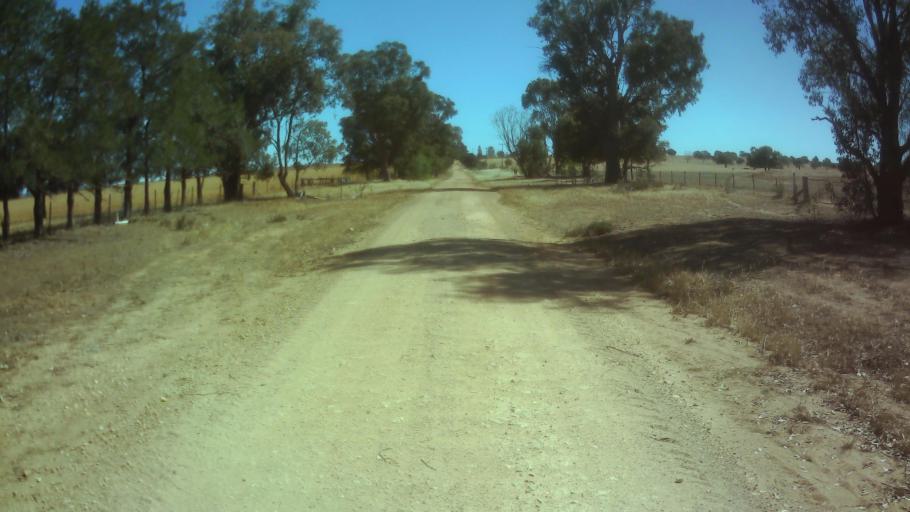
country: AU
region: New South Wales
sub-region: Weddin
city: Grenfell
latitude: -33.9887
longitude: 148.3404
